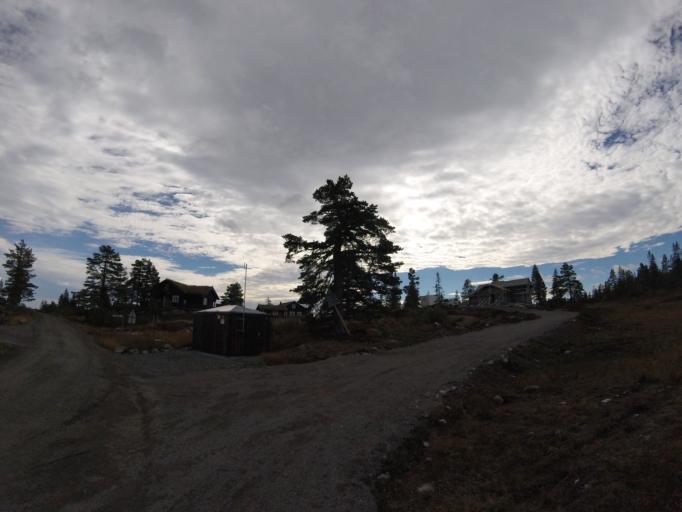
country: NO
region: Buskerud
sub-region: Flesberg
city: Lampeland
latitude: 59.7646
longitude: 9.4661
